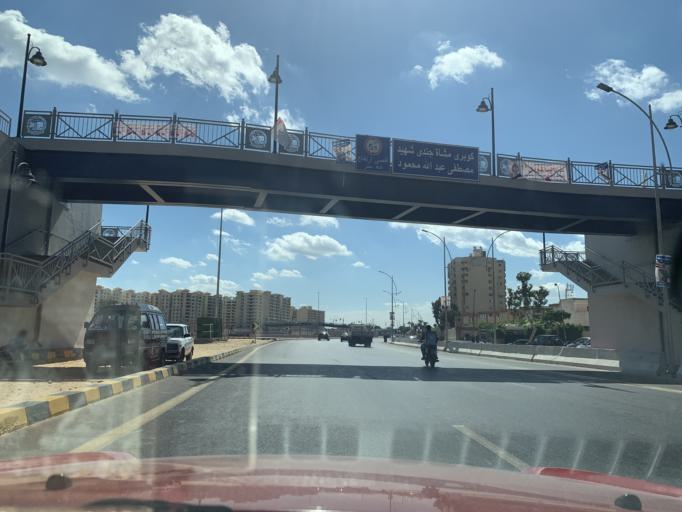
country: EG
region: Alexandria
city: Alexandria
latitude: 31.2071
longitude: 29.9548
